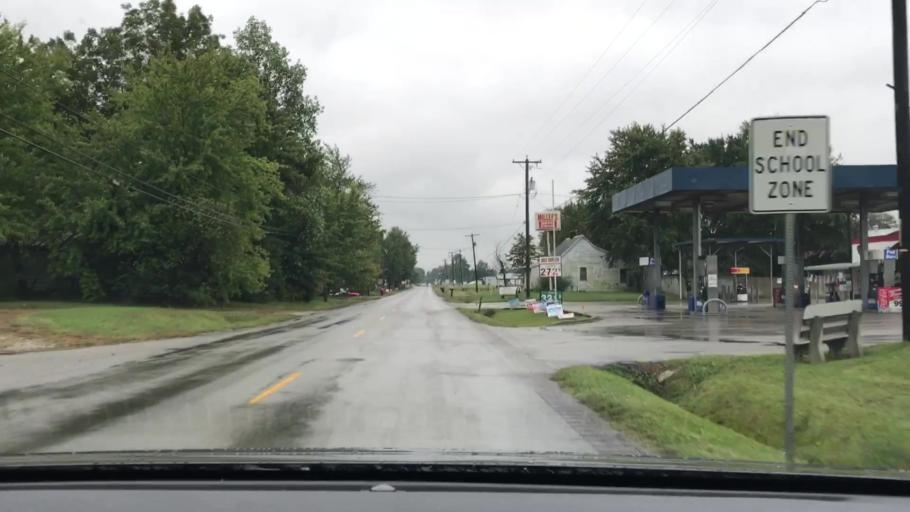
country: US
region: Kentucky
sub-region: McLean County
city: Calhoun
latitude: 37.4101
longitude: -87.2636
